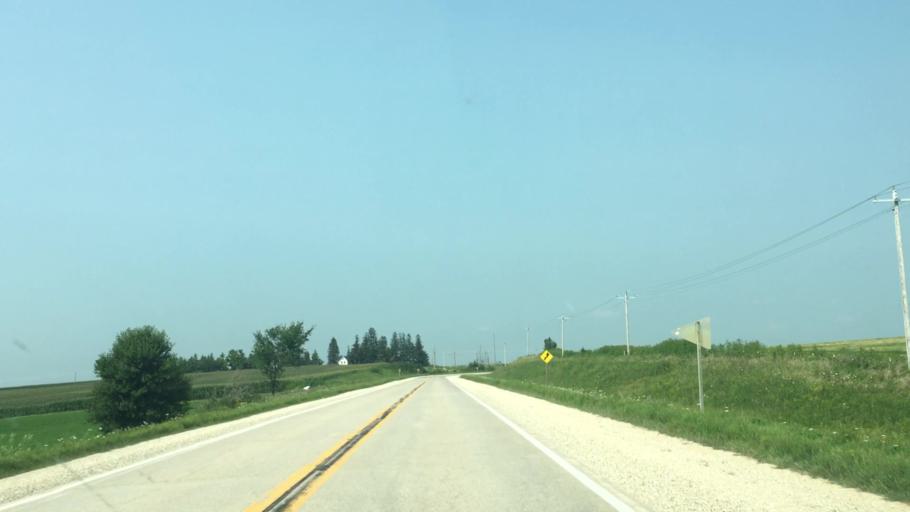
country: US
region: Iowa
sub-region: Fayette County
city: West Union
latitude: 43.1350
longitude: -91.8691
